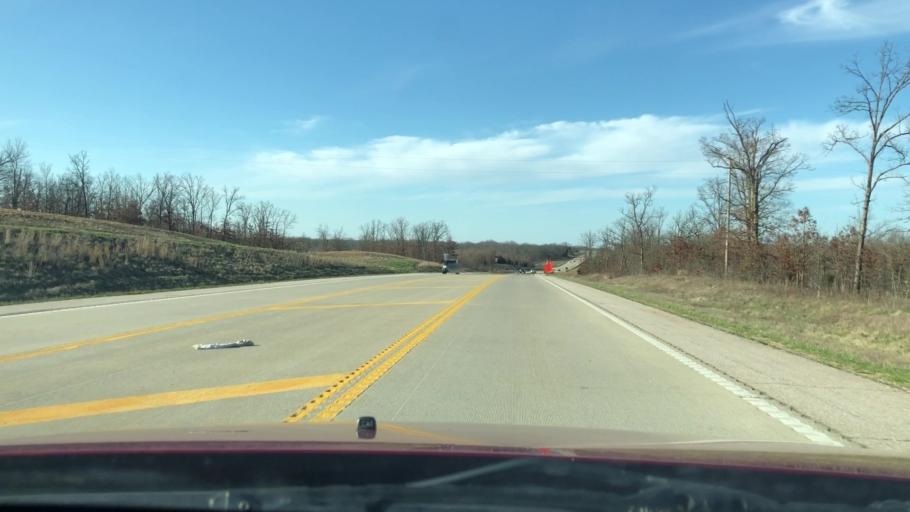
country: US
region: Missouri
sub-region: Camden County
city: Camdenton
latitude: 37.9372
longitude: -92.7153
